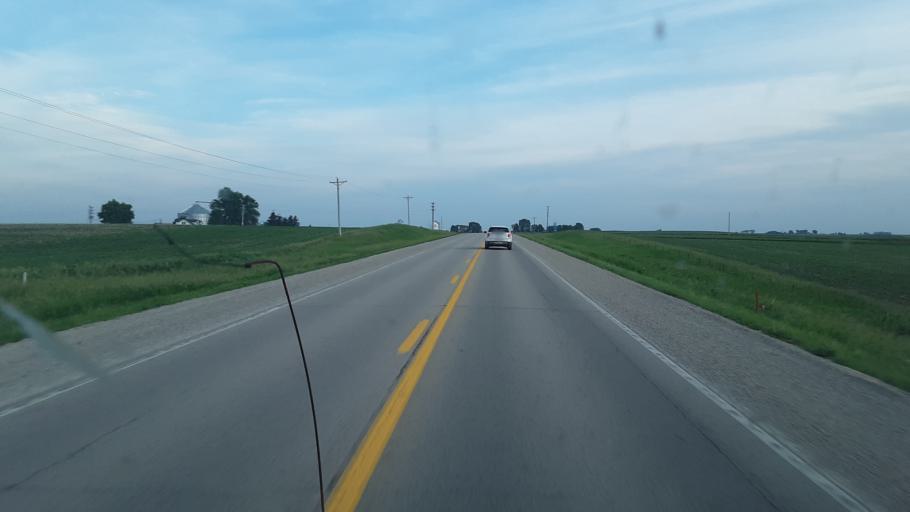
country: US
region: Iowa
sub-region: Benton County
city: Belle Plaine
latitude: 41.8005
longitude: -92.2789
